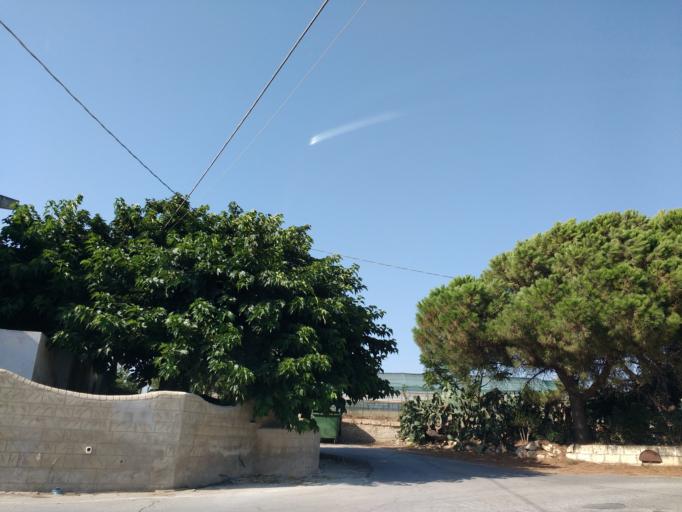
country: IT
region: Sicily
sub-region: Ragusa
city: Cava d'Aliga
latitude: 36.7318
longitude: 14.6938
